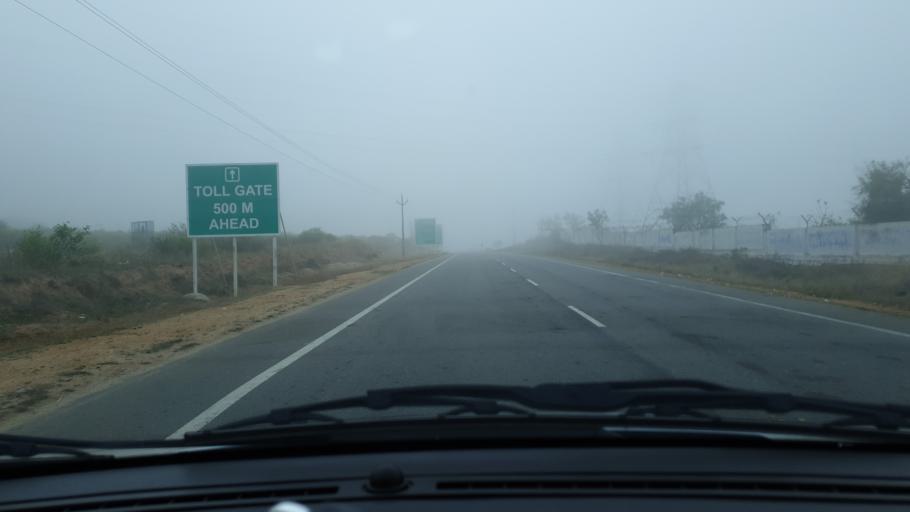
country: IN
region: Telangana
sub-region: Nalgonda
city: Devarkonda
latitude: 16.6165
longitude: 78.6740
